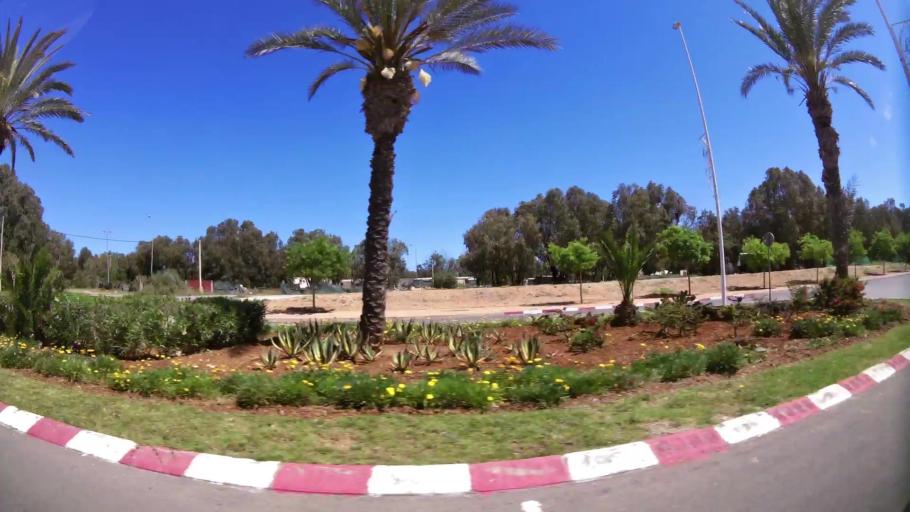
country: MA
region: Oriental
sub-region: Berkane-Taourirt
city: Madagh
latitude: 35.1001
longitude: -2.2871
